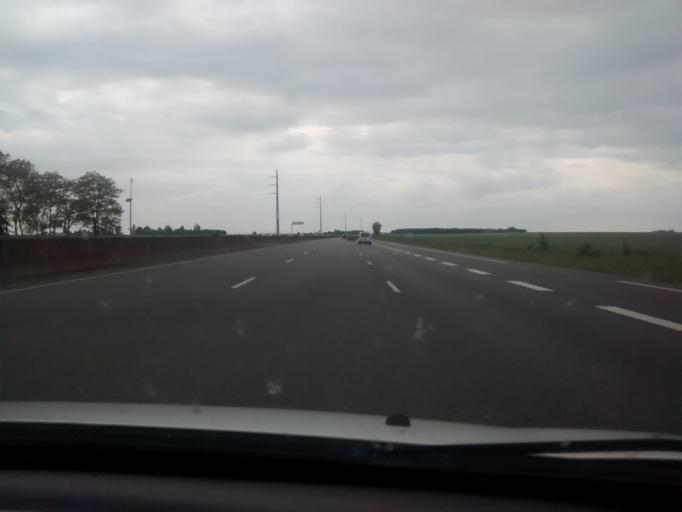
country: FR
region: Centre
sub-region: Departement d'Eure-et-Loir
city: Bailleau-le-Pin
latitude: 48.3226
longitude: 1.3601
